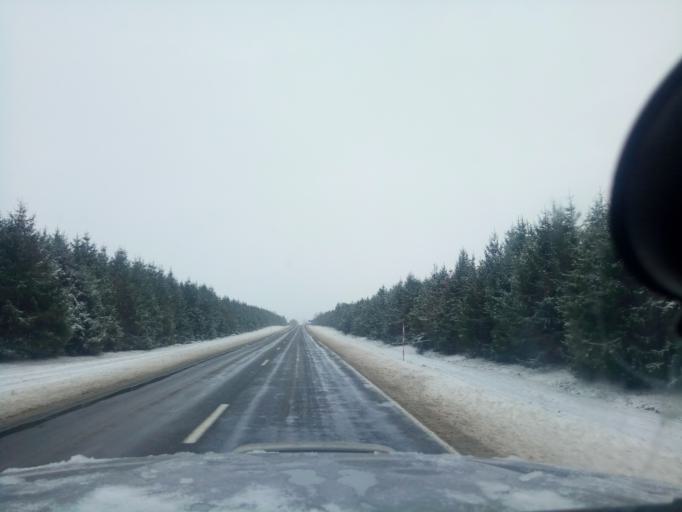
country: BY
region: Minsk
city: Haradzyeya
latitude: 53.3675
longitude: 26.5119
